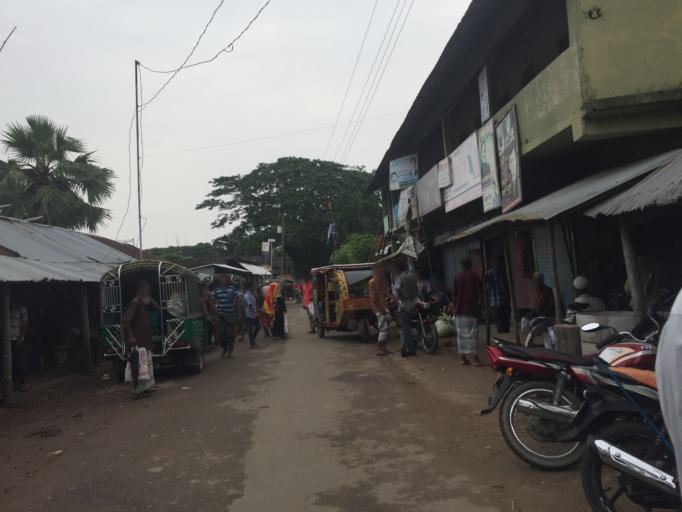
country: BD
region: Barisal
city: Mathba
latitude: 22.2182
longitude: 89.9180
